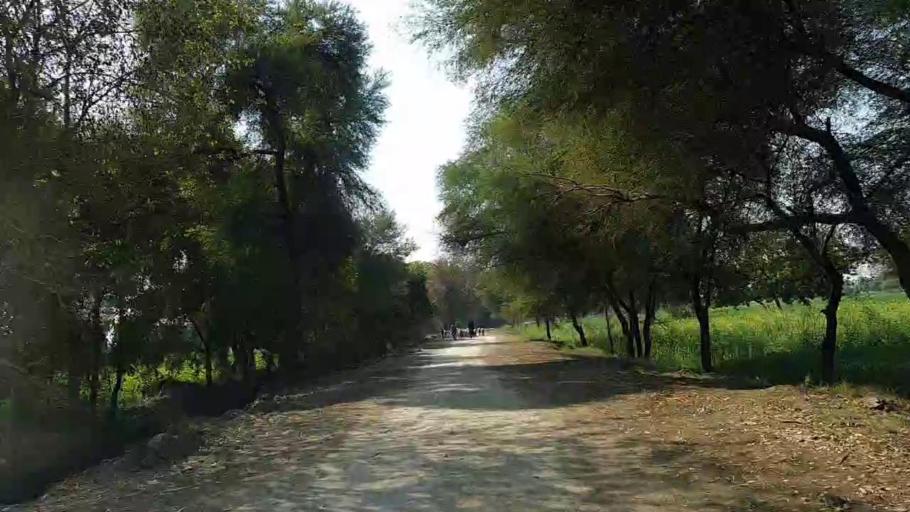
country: PK
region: Sindh
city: Nawabshah
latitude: 26.2463
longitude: 68.4730
